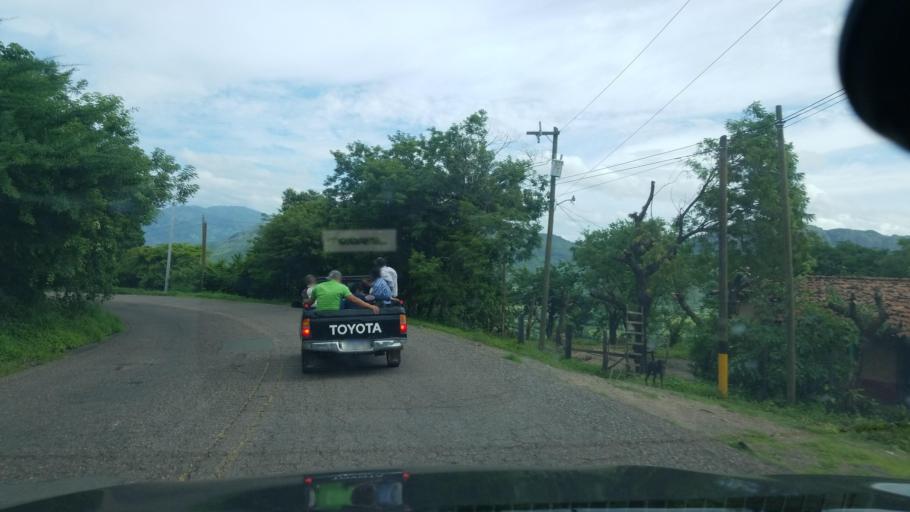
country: HN
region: Choluteca
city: Corpus
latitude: 13.3763
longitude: -87.0556
